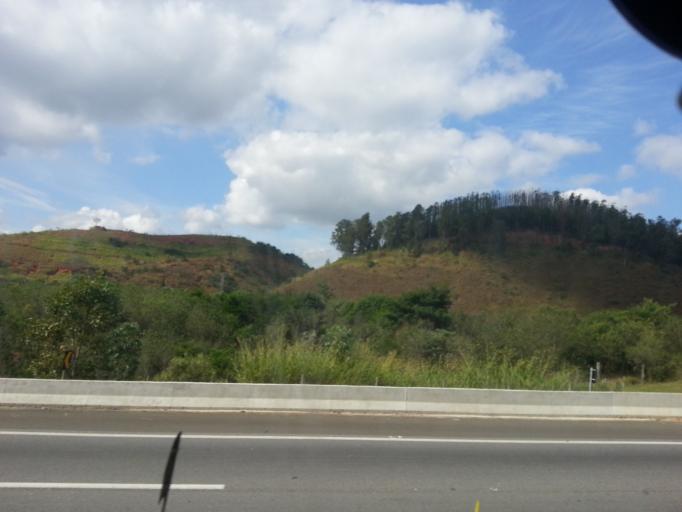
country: BR
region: Sao Paulo
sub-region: Cruzeiro
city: Cruzeiro
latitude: -22.5458
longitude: -44.8035
